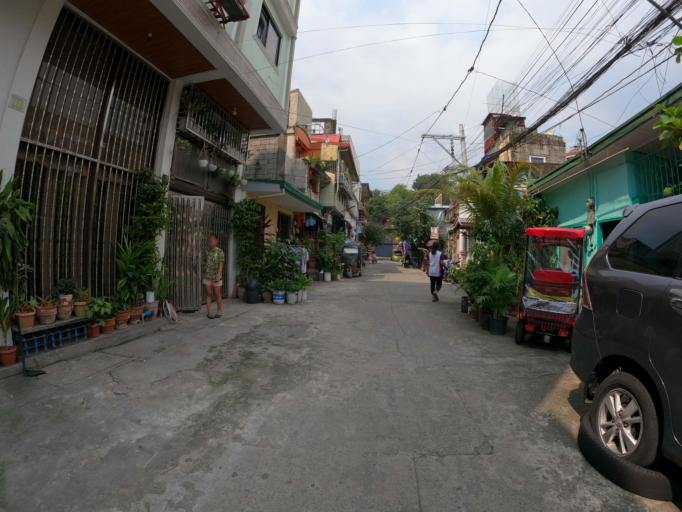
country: PH
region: Metro Manila
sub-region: San Juan
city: San Juan
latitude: 14.5869
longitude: 121.0112
